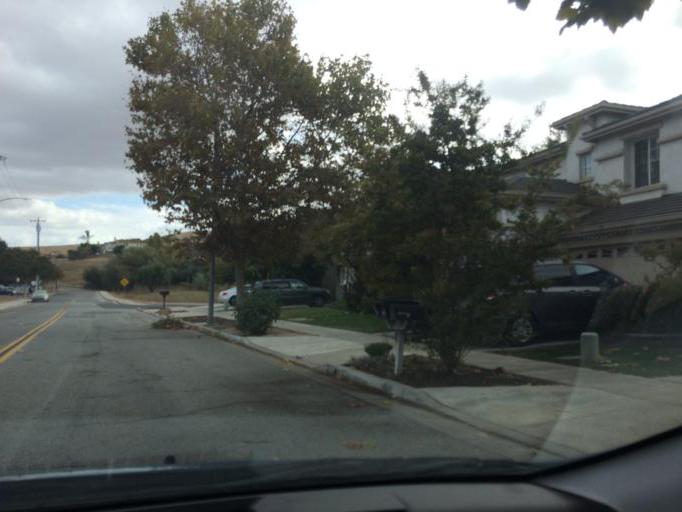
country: US
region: California
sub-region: Santa Clara County
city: Seven Trees
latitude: 37.2990
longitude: -121.8017
